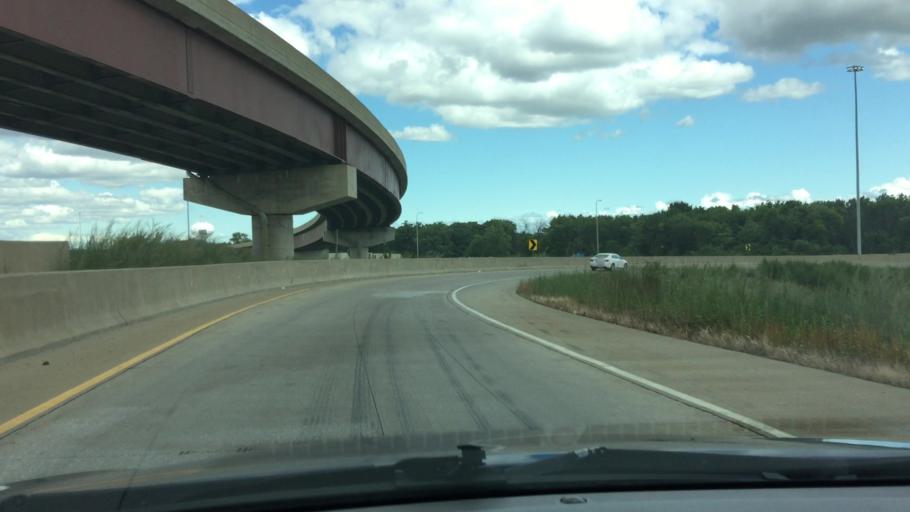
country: US
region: Illinois
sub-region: Cook County
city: Thornton
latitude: 41.5789
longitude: -87.5812
